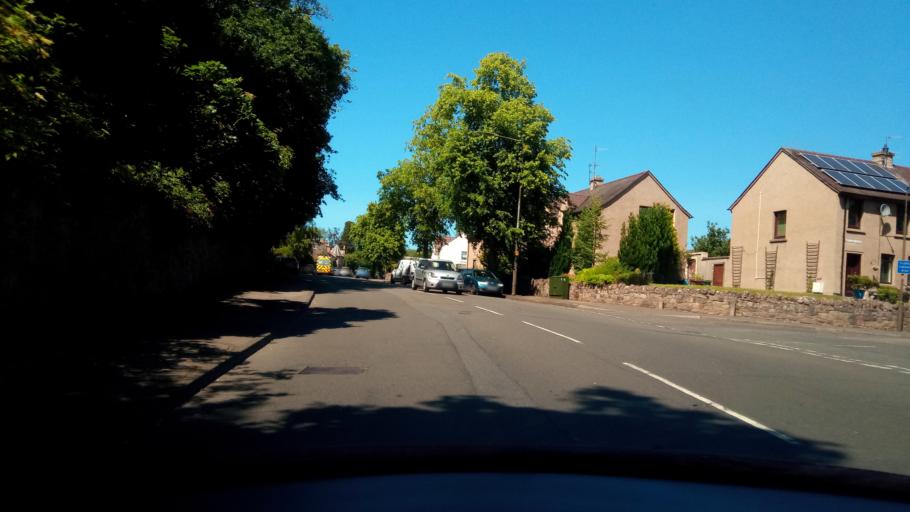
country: GB
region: Scotland
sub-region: East Lothian
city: Haddington
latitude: 55.9583
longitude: -2.7757
